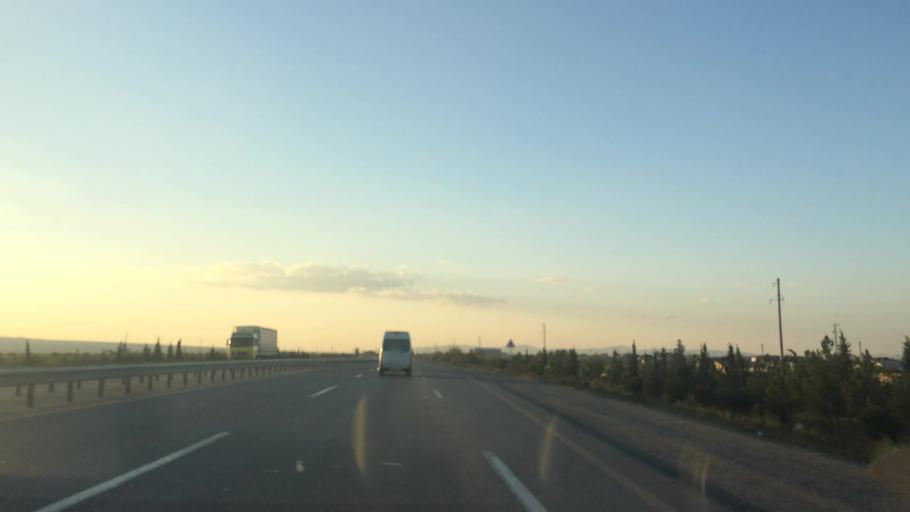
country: AZ
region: Haciqabul
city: Haciqabul
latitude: 40.0033
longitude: 49.1662
